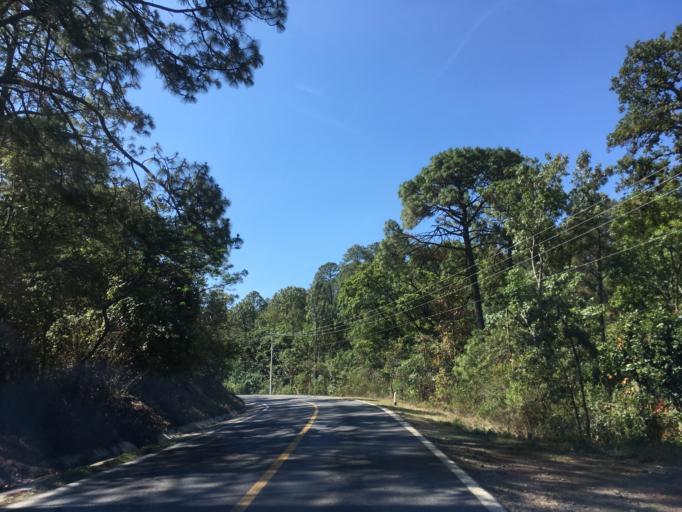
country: MX
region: Michoacan
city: Tzitzio
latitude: 19.6557
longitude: -100.9946
